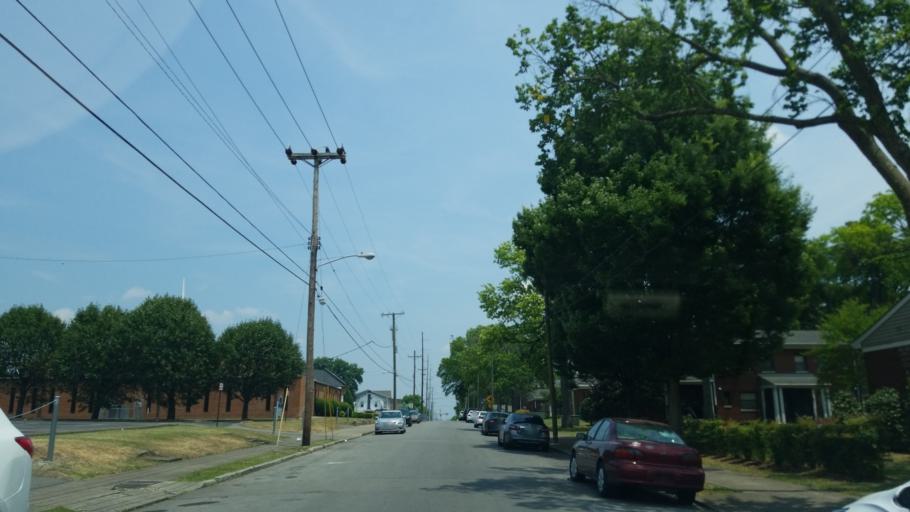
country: US
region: Tennessee
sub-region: Davidson County
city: Nashville
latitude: 36.1674
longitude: -86.8012
